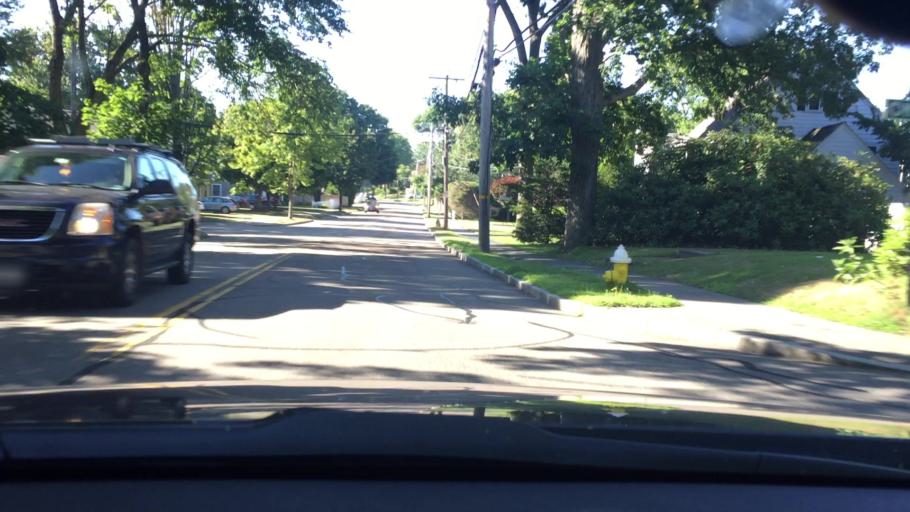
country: US
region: Massachusetts
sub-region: Norfolk County
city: Needham
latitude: 42.2910
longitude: -71.2315
